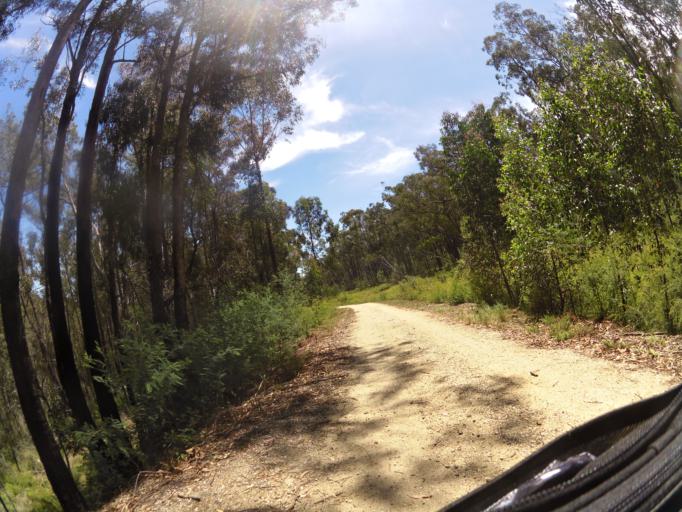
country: AU
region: Victoria
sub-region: East Gippsland
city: Lakes Entrance
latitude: -37.7580
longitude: 147.9303
